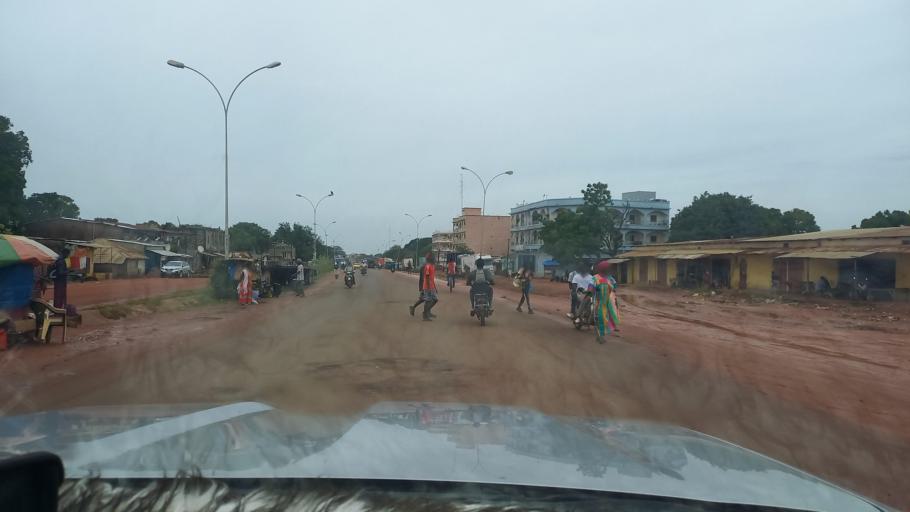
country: SN
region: Ziguinchor
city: Ziguinchor
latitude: 12.5656
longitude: -16.2679
